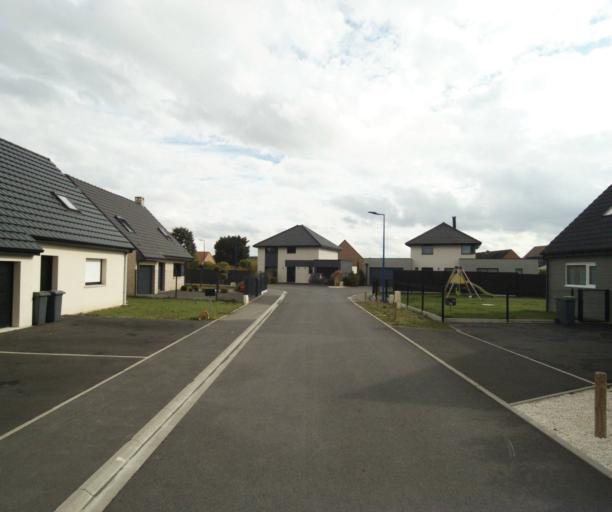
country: FR
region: Nord-Pas-de-Calais
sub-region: Departement du Nord
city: Wavrin
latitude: 50.5721
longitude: 2.9511
